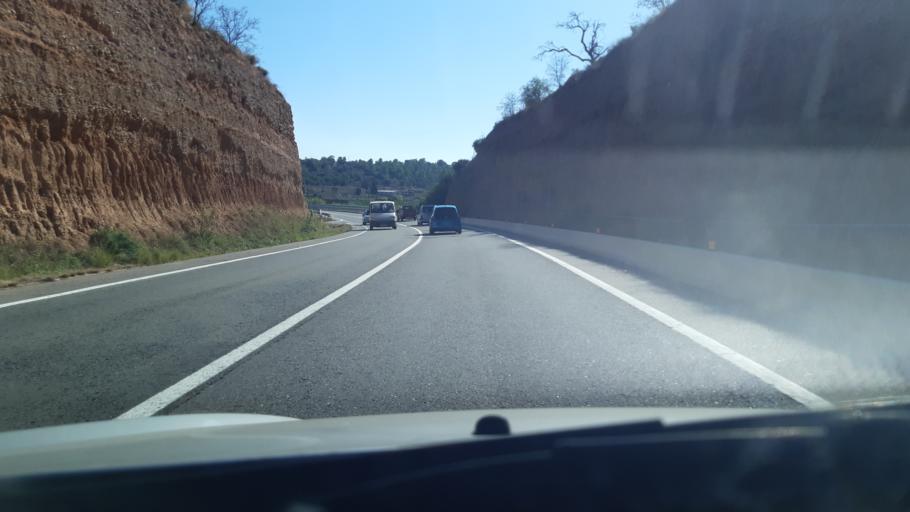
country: ES
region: Catalonia
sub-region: Provincia de Tarragona
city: Tivenys
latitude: 40.8863
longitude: 0.4919
